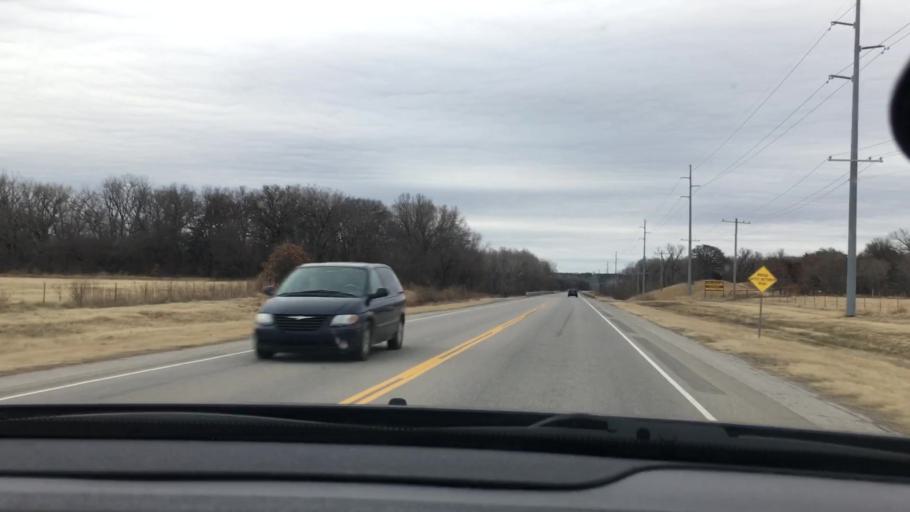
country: US
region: Oklahoma
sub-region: Marshall County
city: Oakland
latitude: 34.2148
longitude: -96.8022
